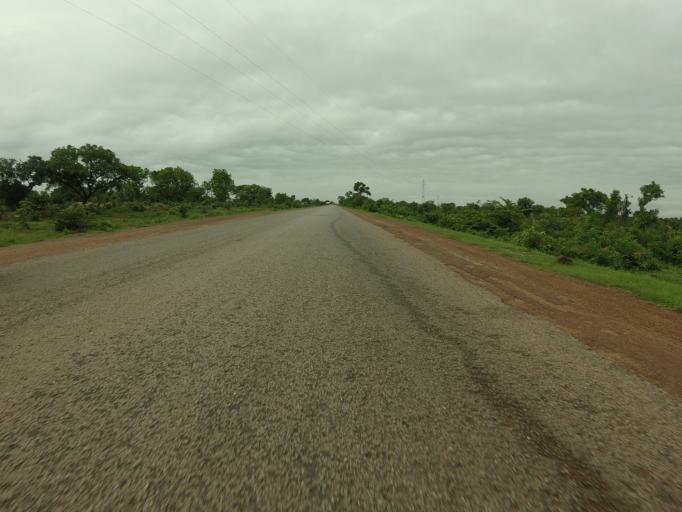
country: GH
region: Northern
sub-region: Yendi
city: Yendi
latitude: 9.4906
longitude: -0.0200
